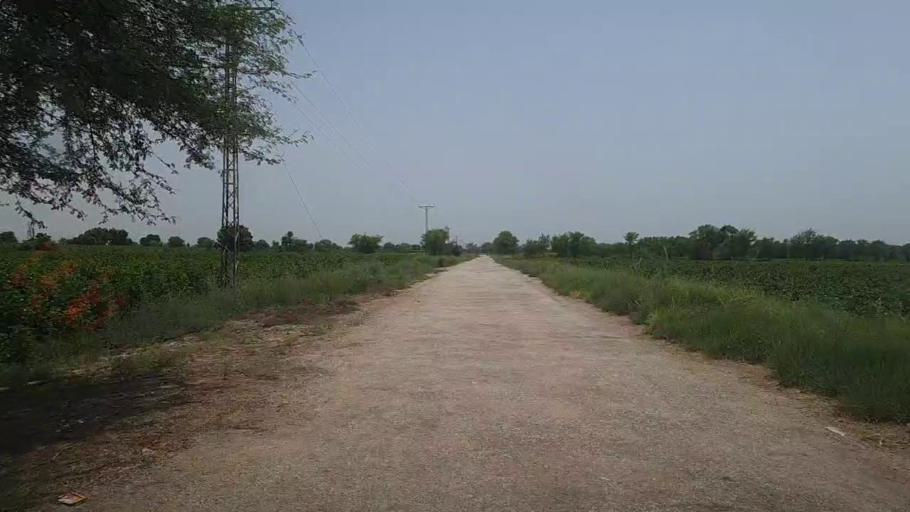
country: PK
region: Sindh
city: Pad Idan
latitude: 26.8387
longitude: 68.3248
